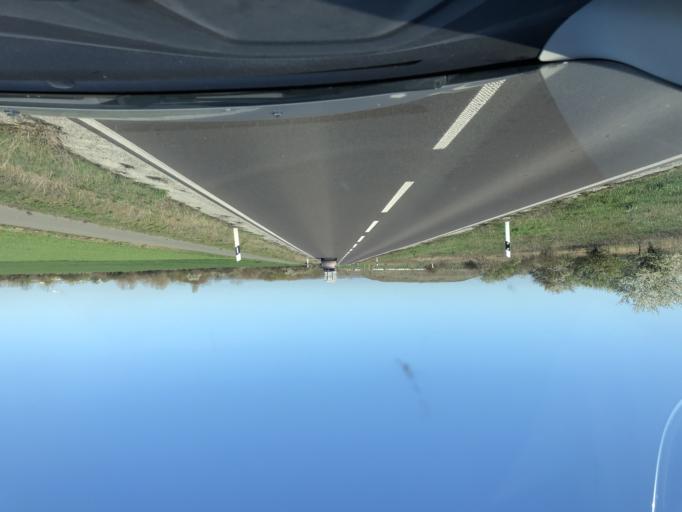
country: DE
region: Saxony-Anhalt
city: Forderstedt
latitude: 51.8504
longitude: 11.6328
